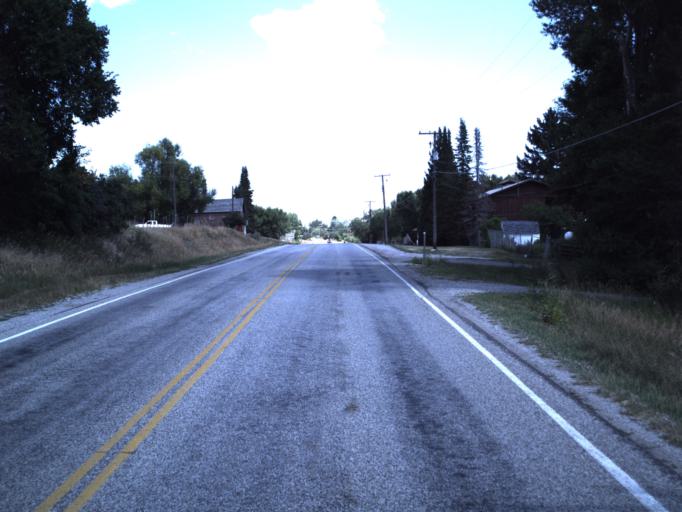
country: US
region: Idaho
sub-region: Bear Lake County
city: Paris
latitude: 41.9948
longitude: -111.4108
